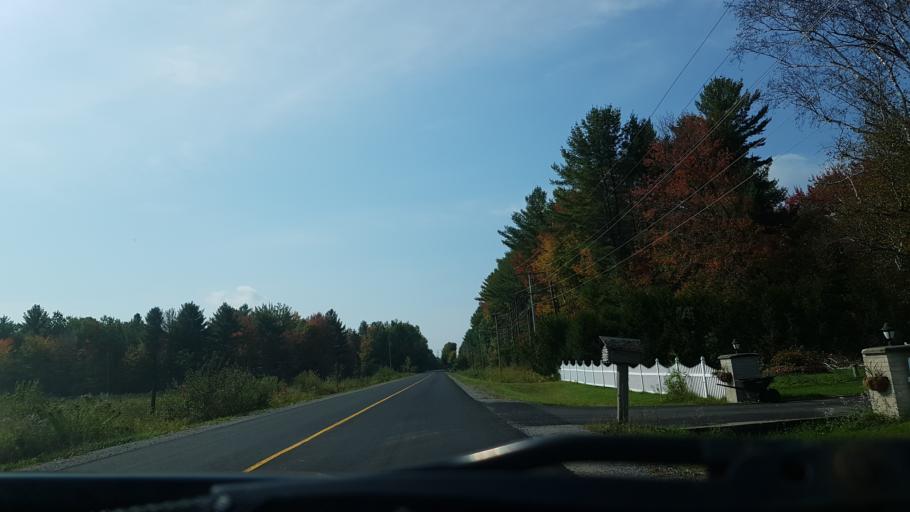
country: CA
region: Ontario
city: Gravenhurst
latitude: 44.8478
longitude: -79.2063
